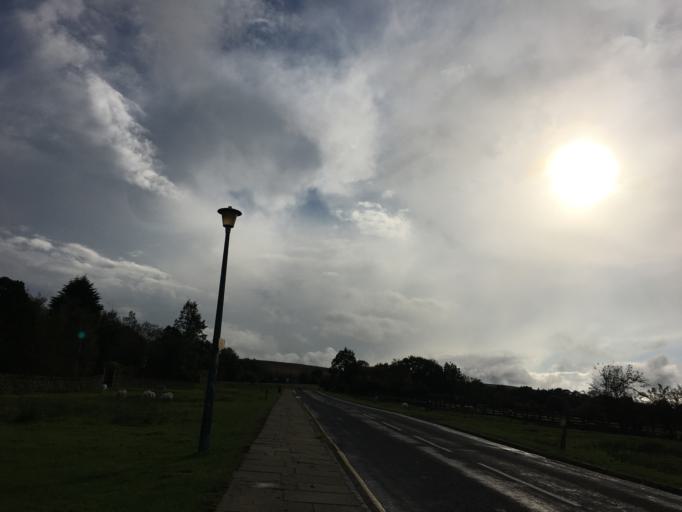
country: GB
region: England
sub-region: North Yorkshire
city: Sleights
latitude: 54.3988
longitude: -0.7217
